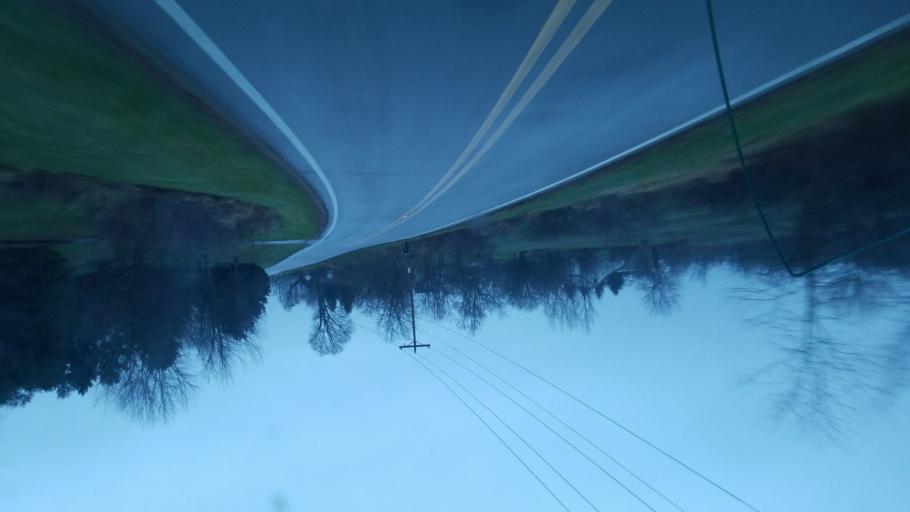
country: US
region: Ohio
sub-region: Delaware County
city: Ashley
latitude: 40.3941
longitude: -82.9476
